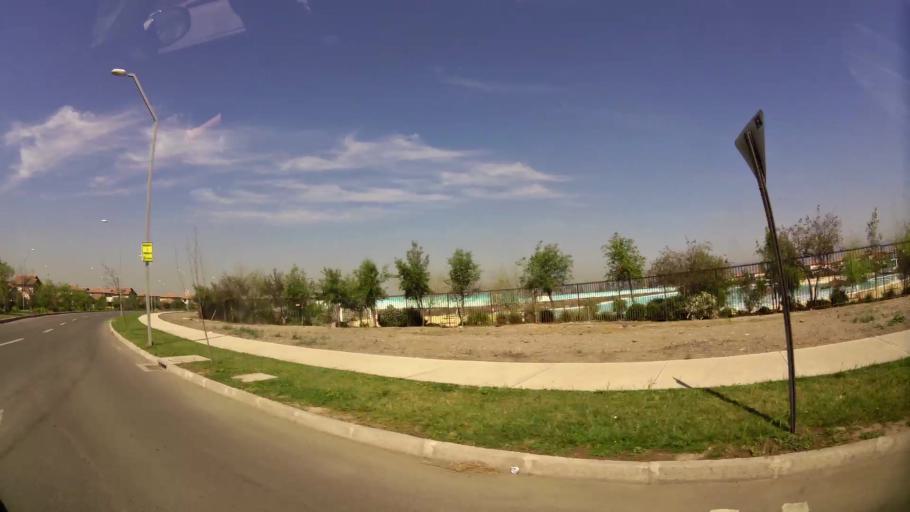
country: CL
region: Santiago Metropolitan
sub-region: Provincia de Talagante
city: Penaflor
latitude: -33.5613
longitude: -70.8289
